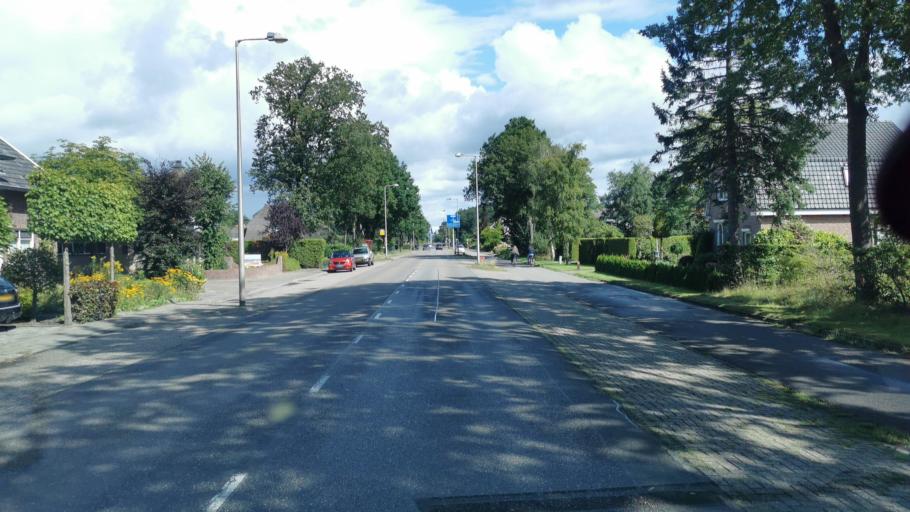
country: NL
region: Overijssel
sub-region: Gemeente Losser
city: Losser
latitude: 52.2621
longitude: 6.9893
